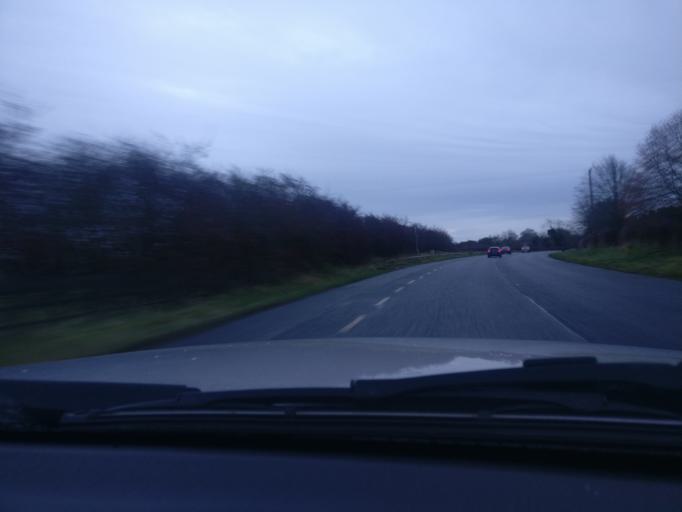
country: IE
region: Leinster
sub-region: An Mhi
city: Kells
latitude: 53.6991
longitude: -6.7901
